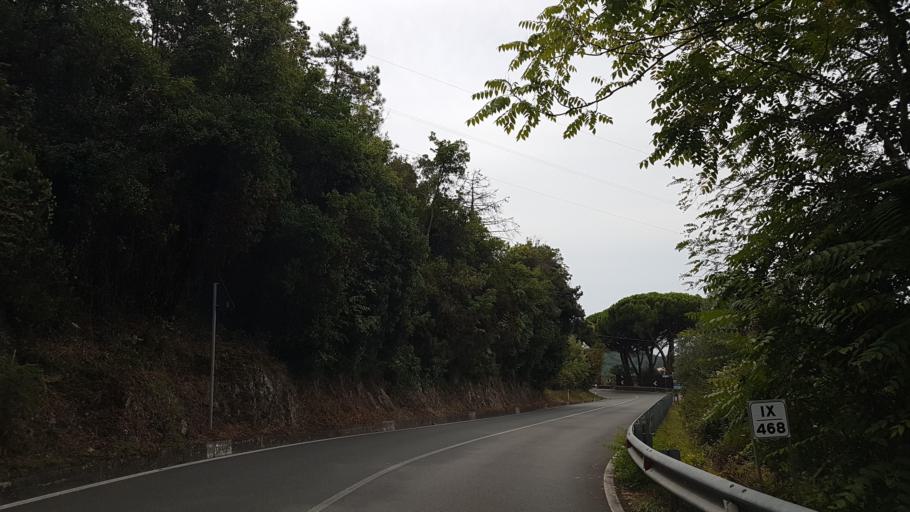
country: IT
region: Liguria
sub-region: Provincia di Genova
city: Casarza Ligure
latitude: 44.2626
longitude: 9.4463
